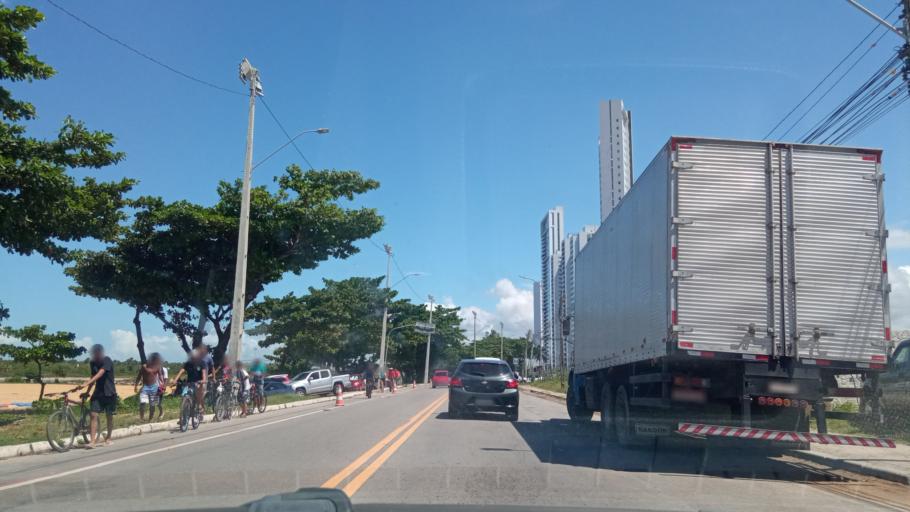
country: BR
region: Pernambuco
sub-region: Jaboatao Dos Guararapes
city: Jaboatao
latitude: -8.2211
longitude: -34.9268
